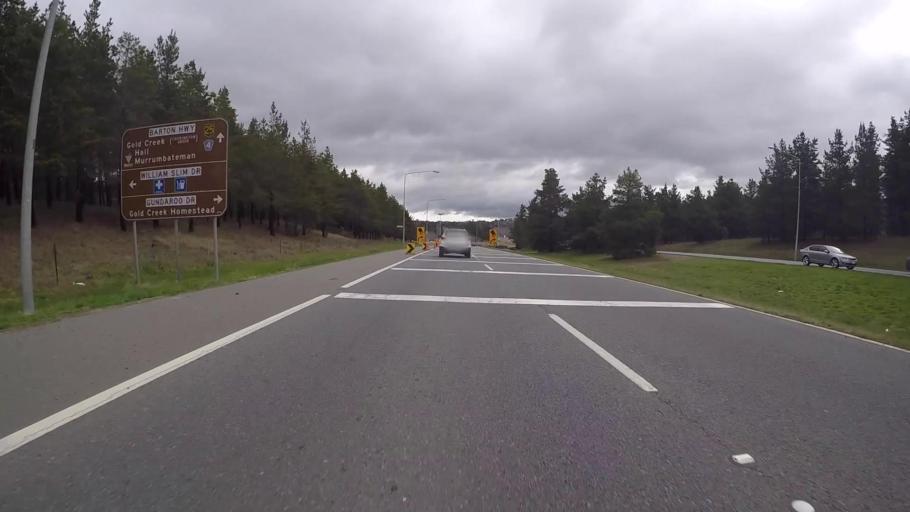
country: AU
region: Australian Capital Territory
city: Kaleen
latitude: -35.2033
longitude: 149.0969
